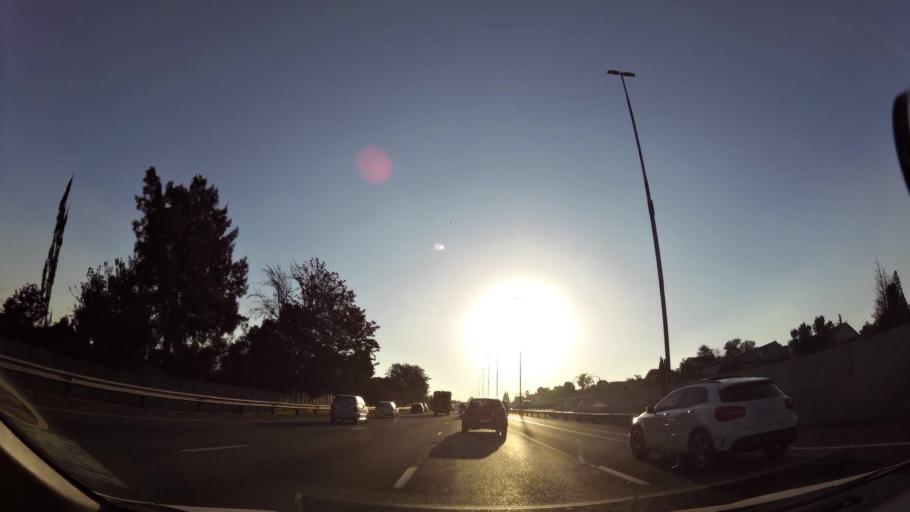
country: ZA
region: Gauteng
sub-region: City of Johannesburg Metropolitan Municipality
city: Johannesburg
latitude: -26.2700
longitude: 28.0387
